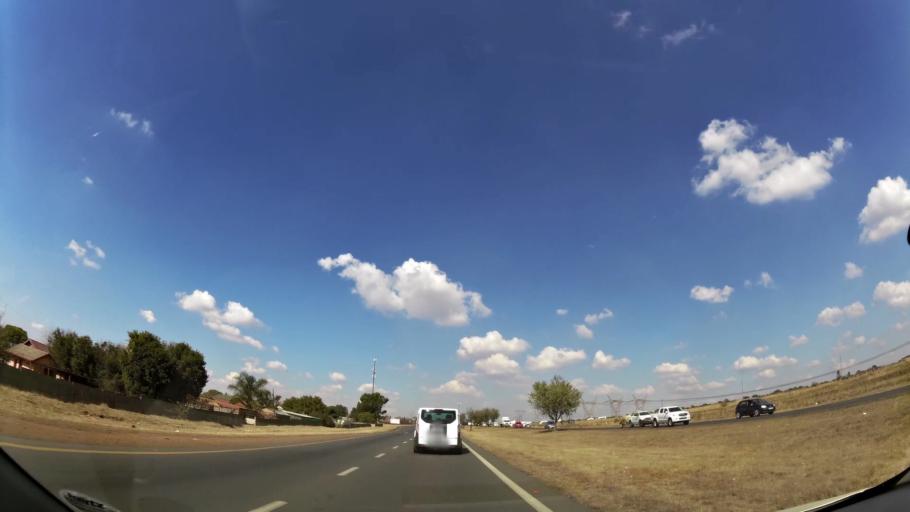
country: ZA
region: Mpumalanga
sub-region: Nkangala District Municipality
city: Witbank
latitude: -25.9382
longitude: 29.2402
